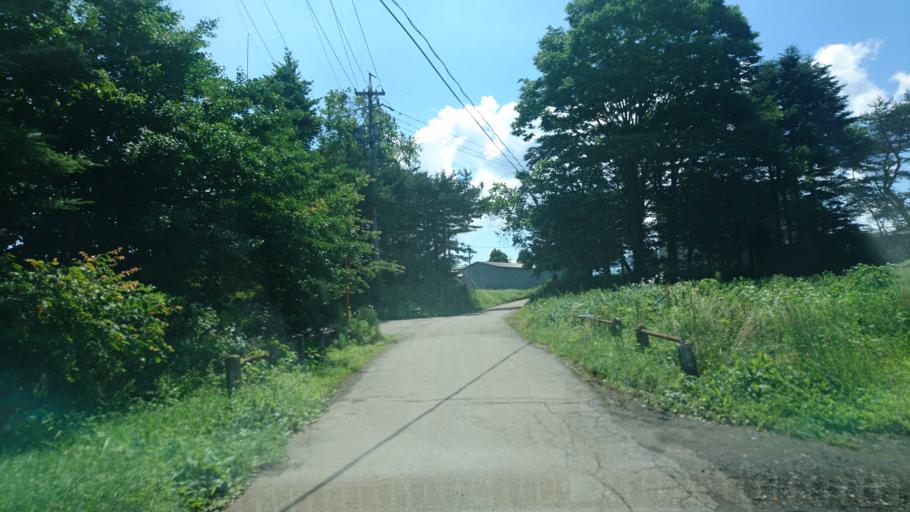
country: JP
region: Nagano
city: Saku
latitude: 36.3149
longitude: 138.5881
